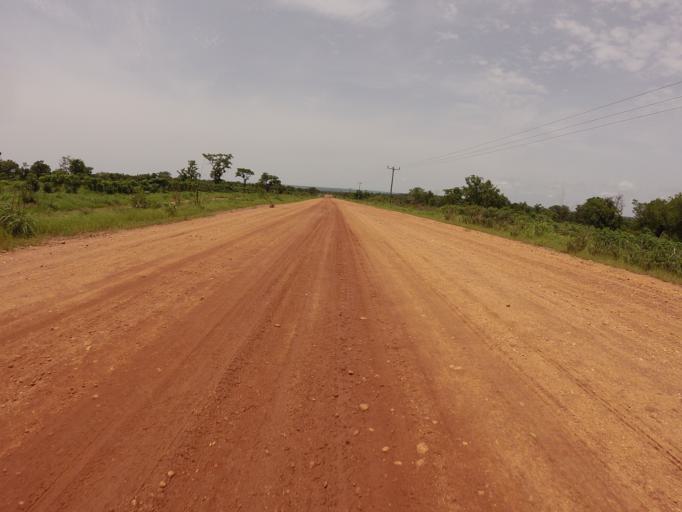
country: GH
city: Kpandae
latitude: 8.7273
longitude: 0.1154
